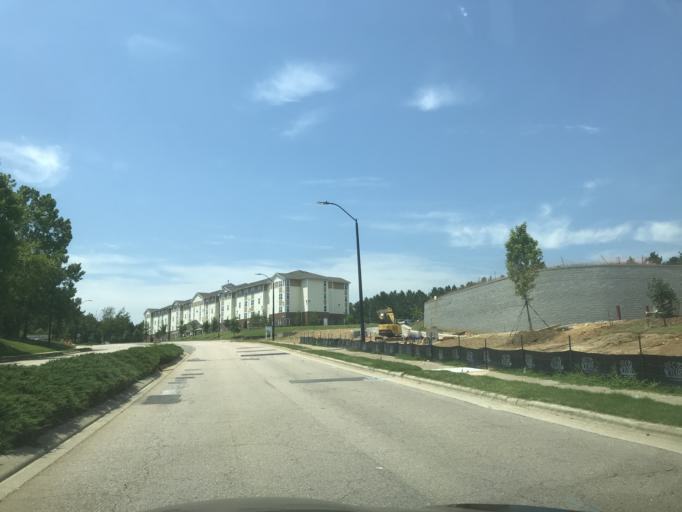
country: US
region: North Carolina
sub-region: Wake County
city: Wake Forest
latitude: 35.9432
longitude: -78.5598
